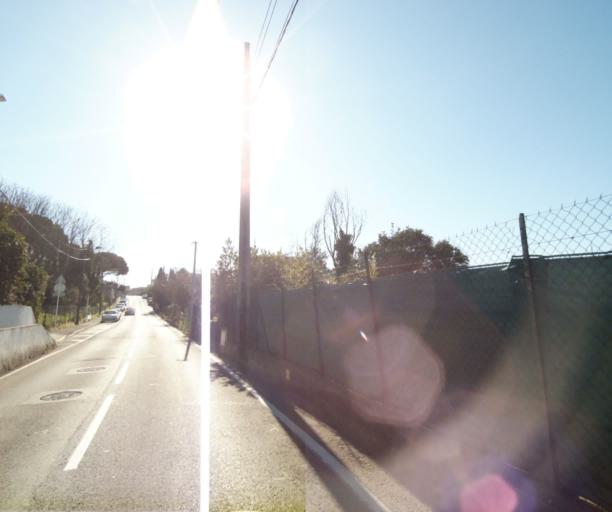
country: FR
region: Provence-Alpes-Cote d'Azur
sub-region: Departement des Alpes-Maritimes
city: Antibes
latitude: 43.5909
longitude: 7.1108
